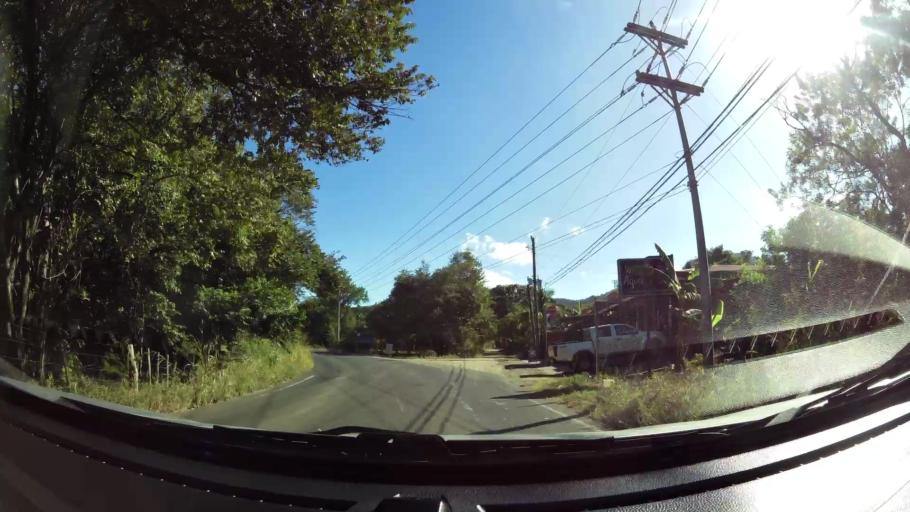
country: CR
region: Guanacaste
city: Sardinal
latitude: 10.4108
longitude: -85.7874
